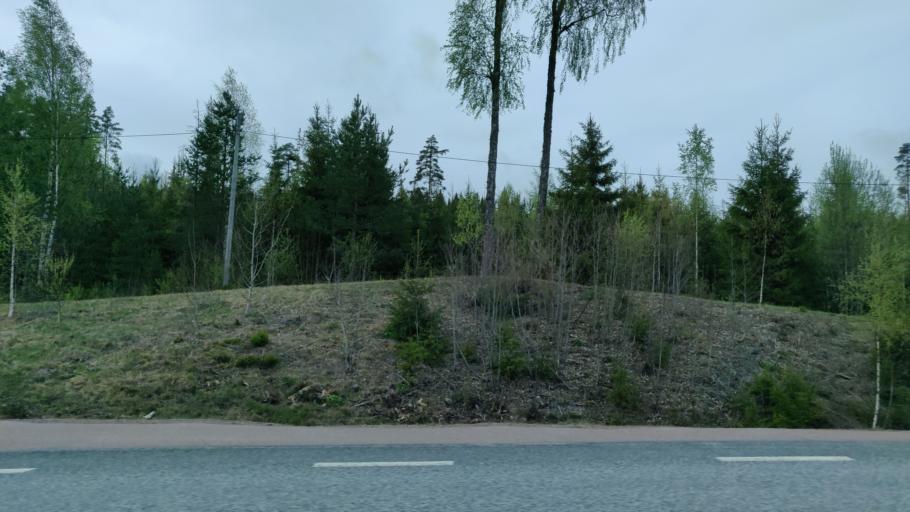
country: SE
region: Vaermland
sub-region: Munkfors Kommun
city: Munkfors
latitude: 59.7789
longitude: 13.4562
